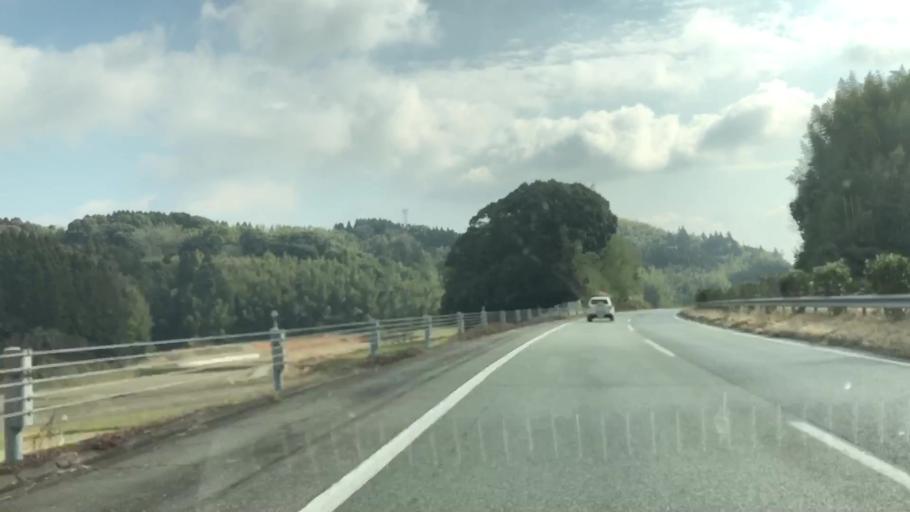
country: JP
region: Kumamoto
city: Yamaga
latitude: 33.0288
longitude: 130.5760
